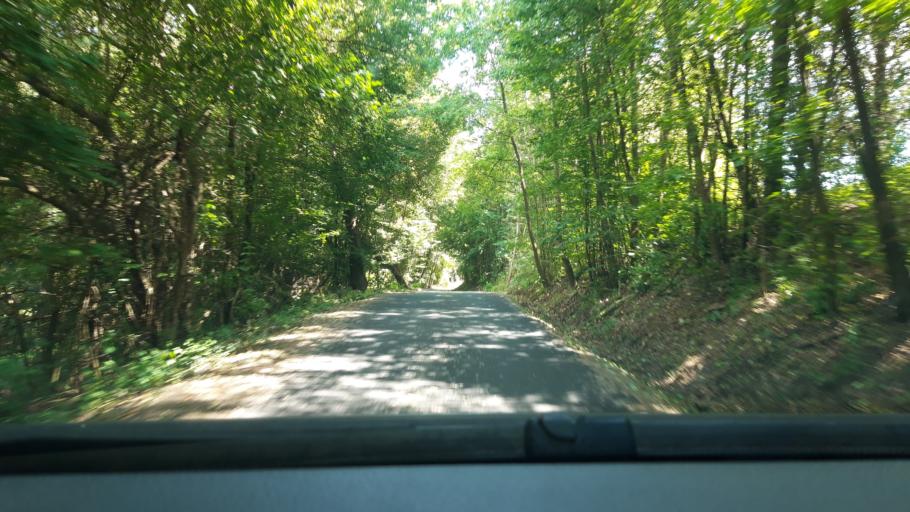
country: HU
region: Nograd
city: Somoskoujfalu
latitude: 48.1805
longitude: 19.8519
